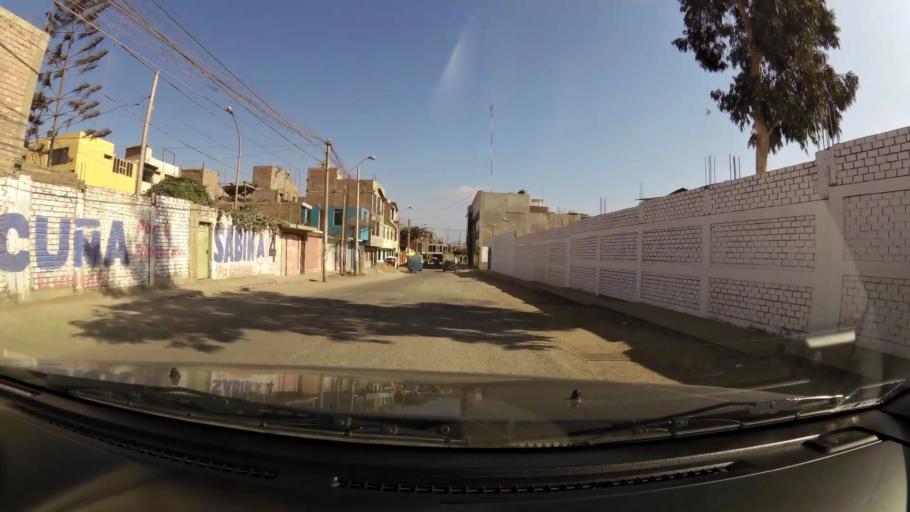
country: PE
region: Ica
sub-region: Provincia de Chincha
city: Chincha Alta
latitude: -13.4147
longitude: -76.1280
